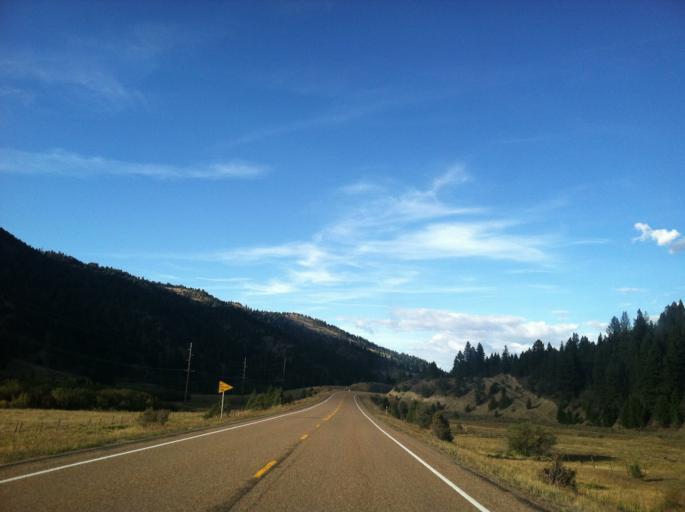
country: US
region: Montana
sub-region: Granite County
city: Philipsburg
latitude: 46.4143
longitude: -113.2875
